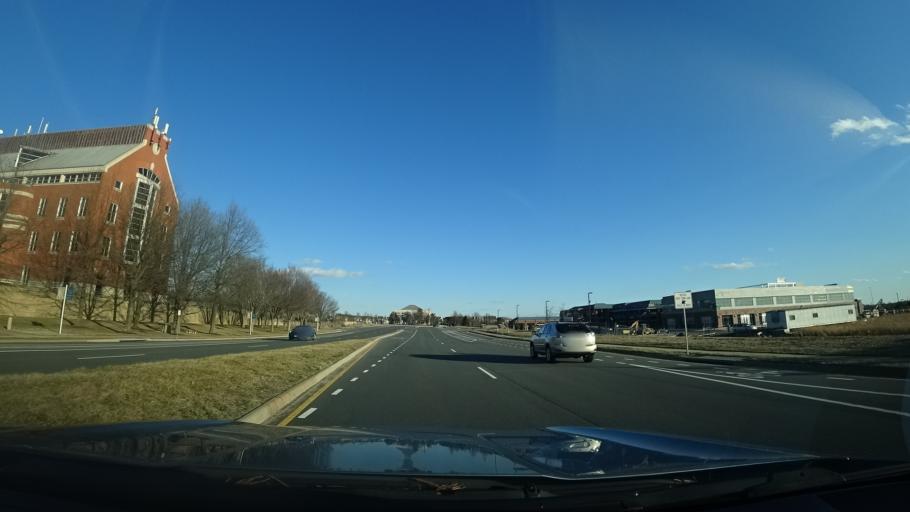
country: US
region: Virginia
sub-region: Loudoun County
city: University Center
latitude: 39.0597
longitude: -77.4473
